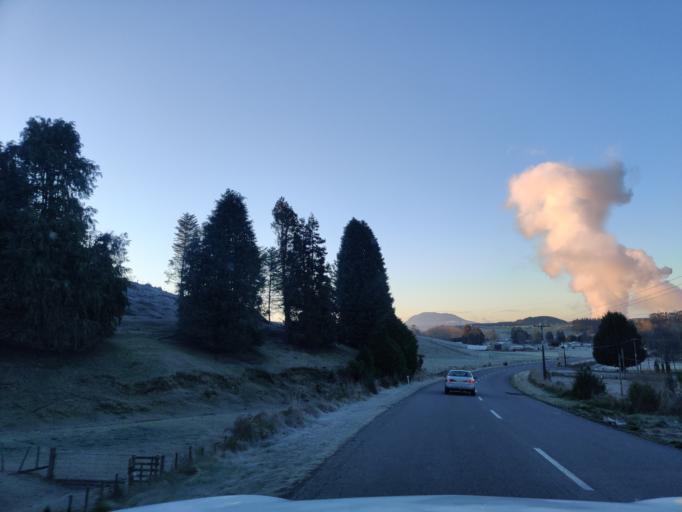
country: NZ
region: Waikato
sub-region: Taupo District
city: Taupo
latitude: -38.5968
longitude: 176.0333
